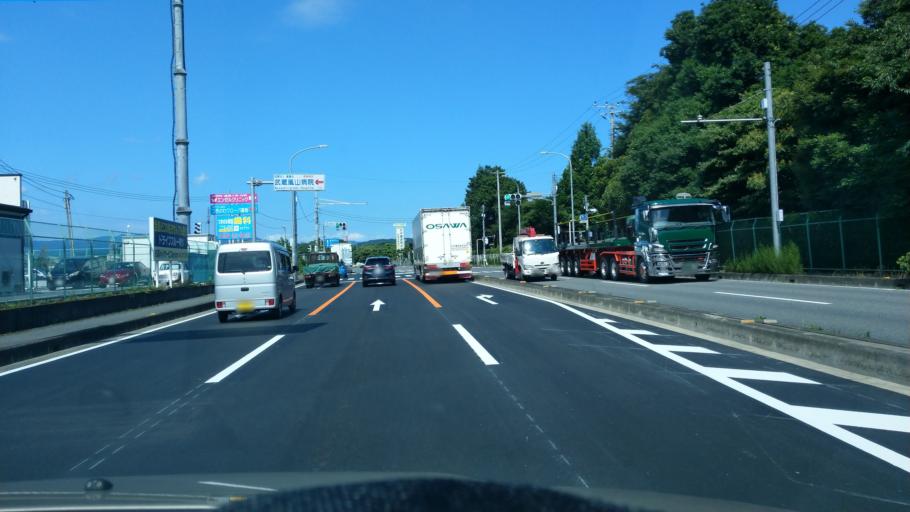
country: JP
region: Saitama
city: Ogawa
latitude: 36.0400
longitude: 139.3476
